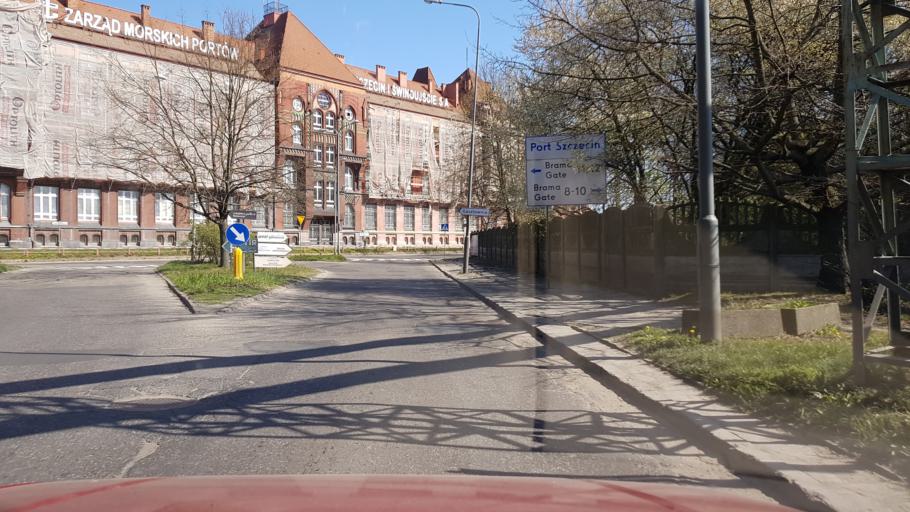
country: PL
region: West Pomeranian Voivodeship
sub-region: Szczecin
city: Szczecin
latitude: 53.4172
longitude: 14.5703
